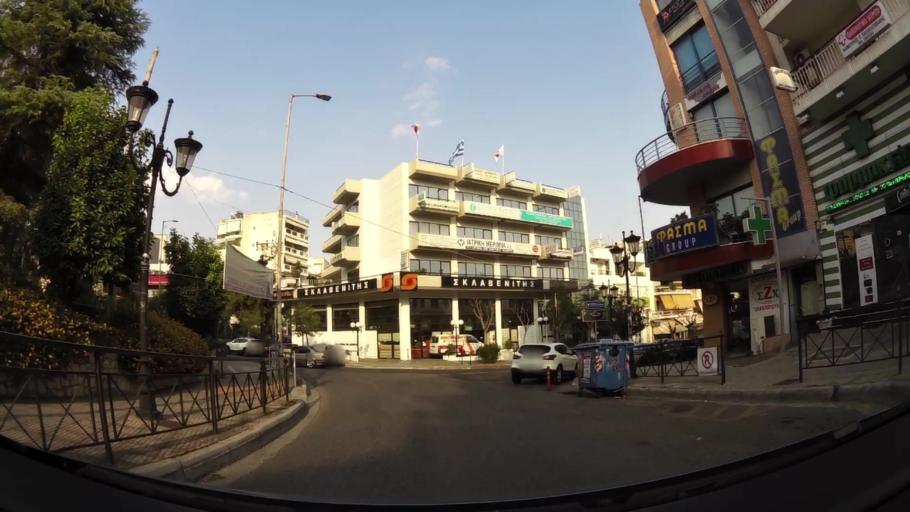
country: GR
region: Attica
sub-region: Nomarchia Athinas
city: Petroupolis
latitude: 38.0421
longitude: 23.6838
